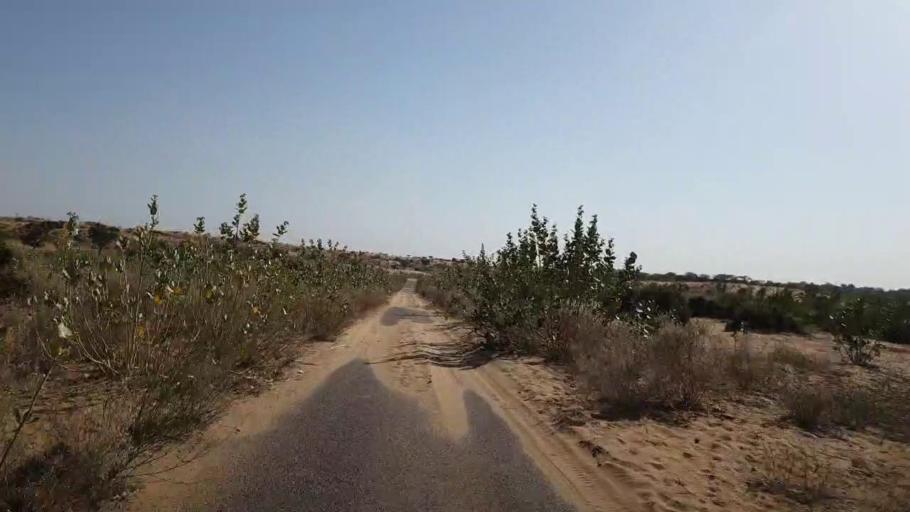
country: PK
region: Sindh
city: Nabisar
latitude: 25.0515
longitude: 70.0218
